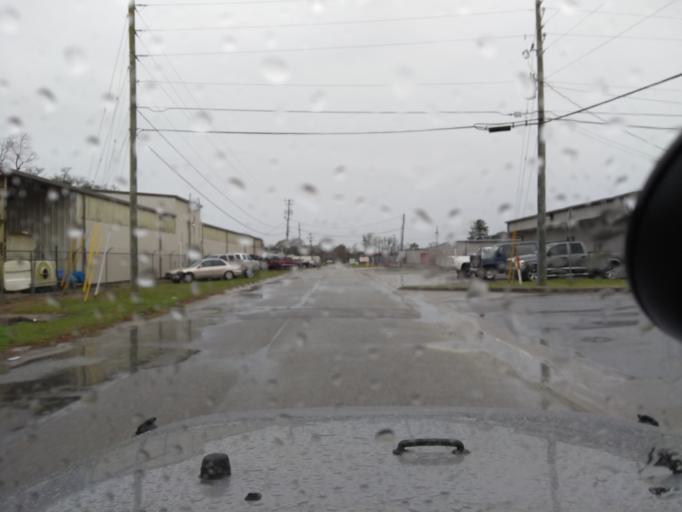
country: US
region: Georgia
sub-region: Chatham County
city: Garden City
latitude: 32.0886
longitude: -81.1597
